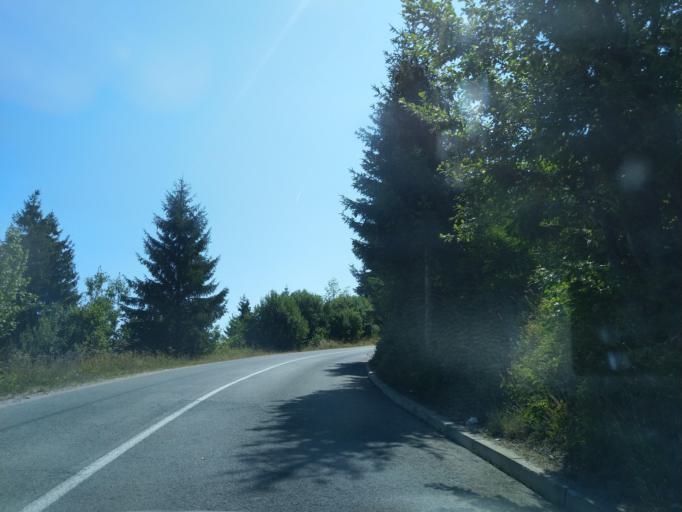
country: RS
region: Central Serbia
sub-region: Zlatiborski Okrug
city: Nova Varos
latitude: 43.4069
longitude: 19.8425
